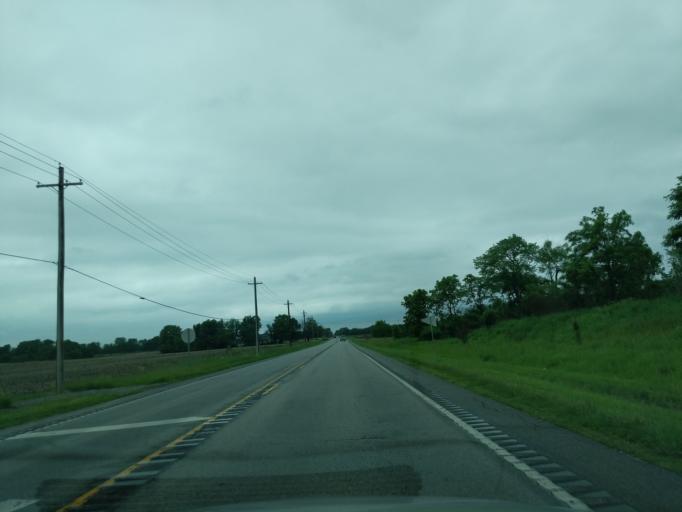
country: US
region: Indiana
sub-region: Hamilton County
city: Cicero
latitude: 40.1075
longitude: -86.0137
